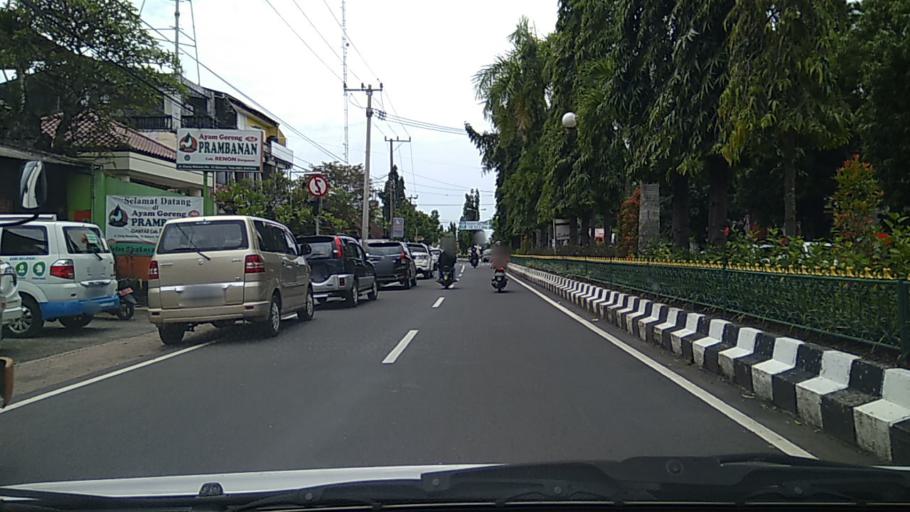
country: ID
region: Bali
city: Banjar Kelodan
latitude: -8.5390
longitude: 115.3227
